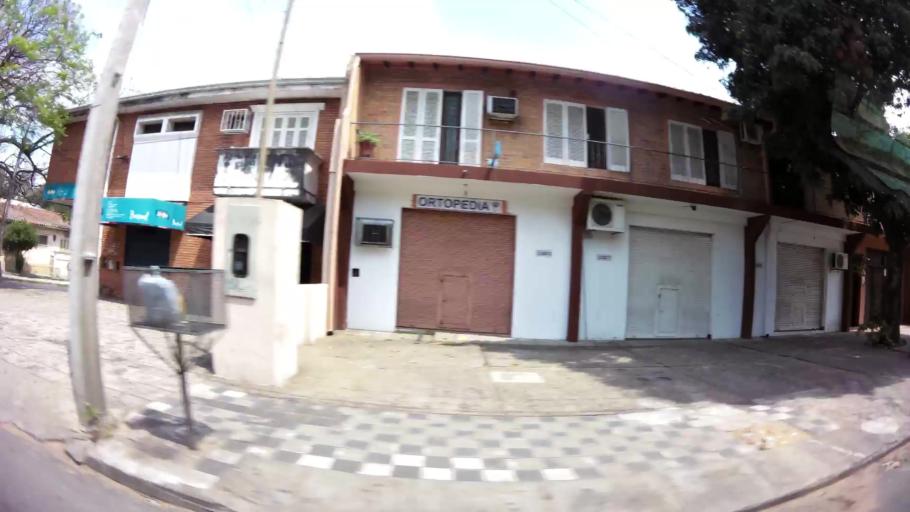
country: PY
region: Asuncion
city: Asuncion
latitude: -25.2737
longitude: -57.5850
